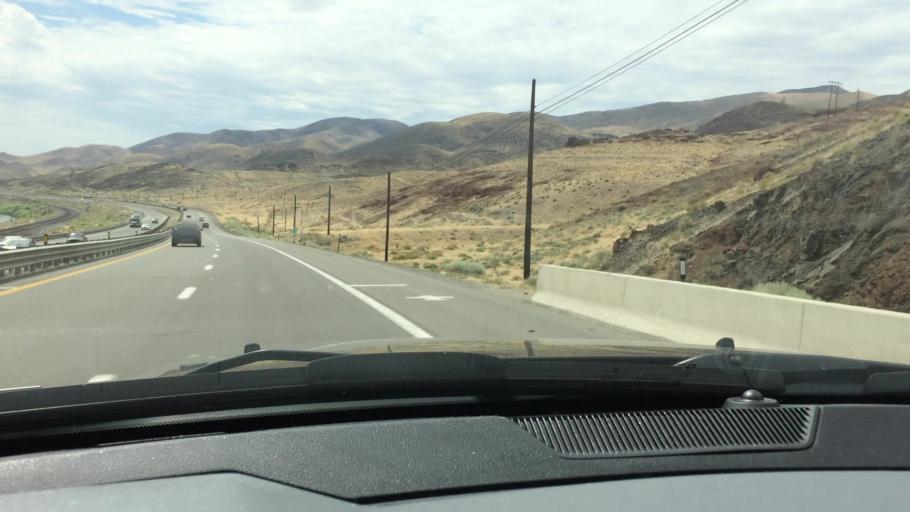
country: US
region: Nevada
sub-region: Lyon County
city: Fernley
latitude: 39.5911
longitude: -119.4064
